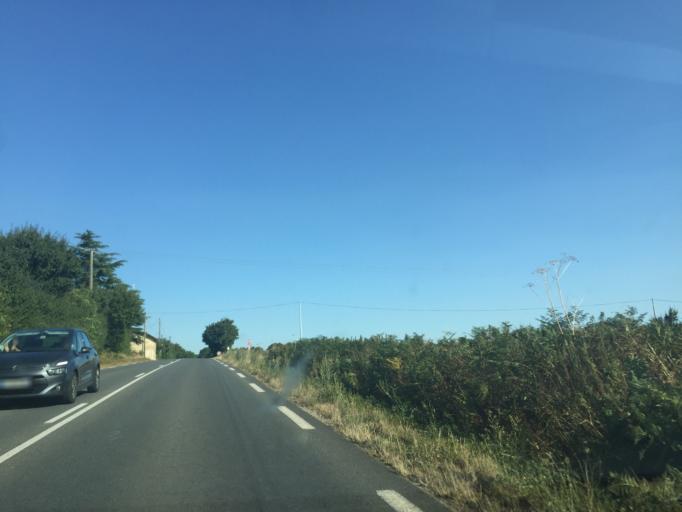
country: FR
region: Poitou-Charentes
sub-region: Departement des Deux-Sevres
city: Melle
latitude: 46.2006
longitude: -0.0837
